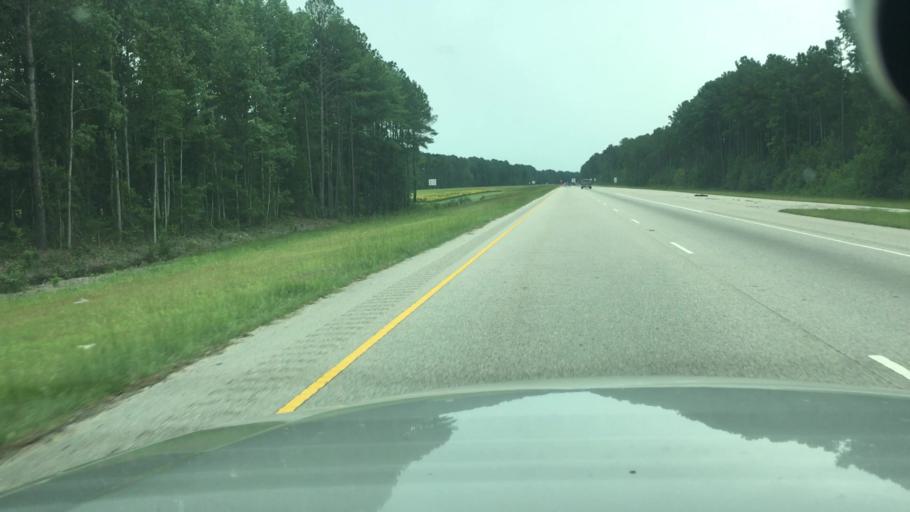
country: US
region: North Carolina
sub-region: Cumberland County
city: Fayetteville
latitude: 34.9730
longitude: -78.8544
